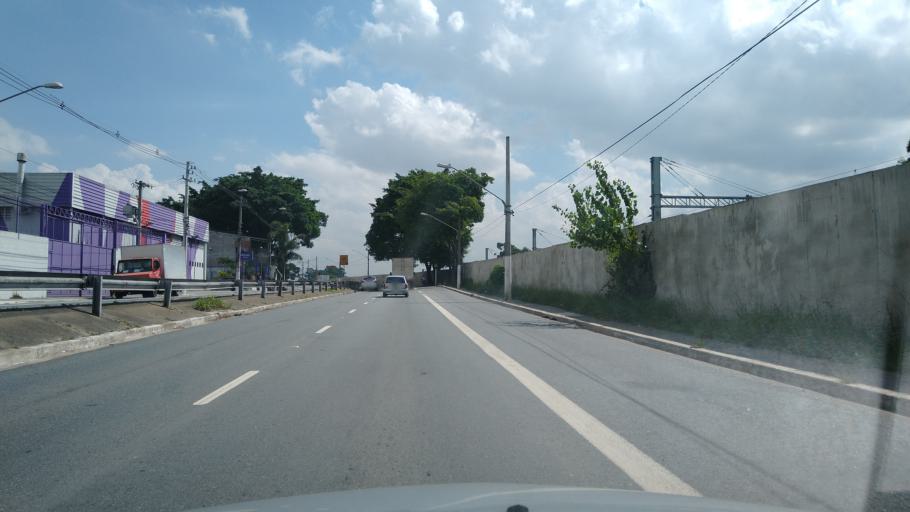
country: BR
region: Sao Paulo
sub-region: Guarulhos
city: Guarulhos
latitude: -23.4962
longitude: -46.5129
